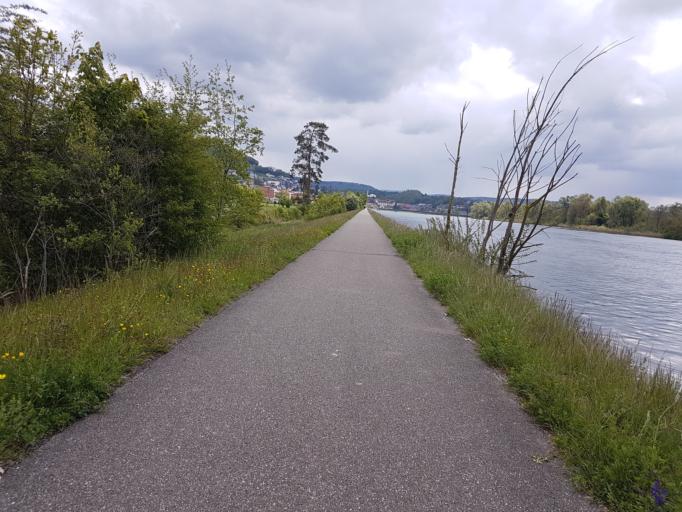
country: CH
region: Aargau
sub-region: Bezirk Zurzach
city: Klingnau
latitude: 47.5800
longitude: 8.2451
